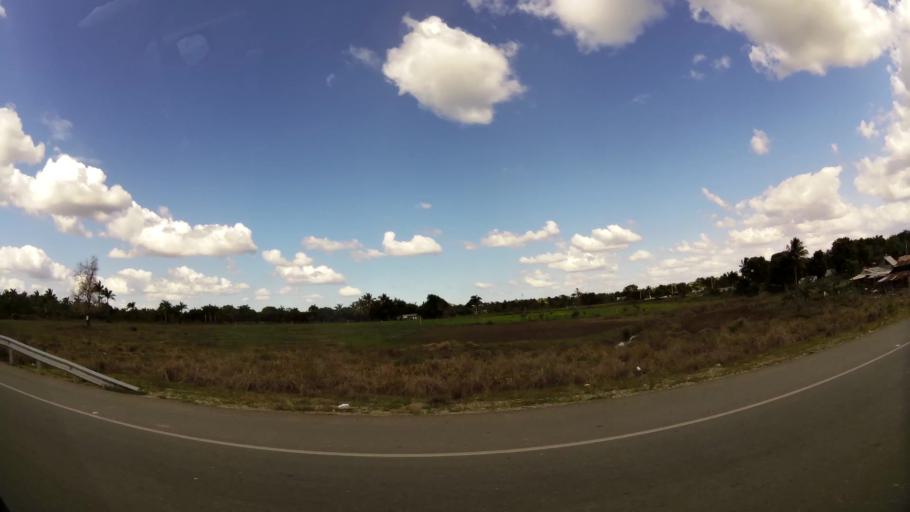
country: DO
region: Santo Domingo
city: Santo Domingo Oeste
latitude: 18.5294
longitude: -70.0691
